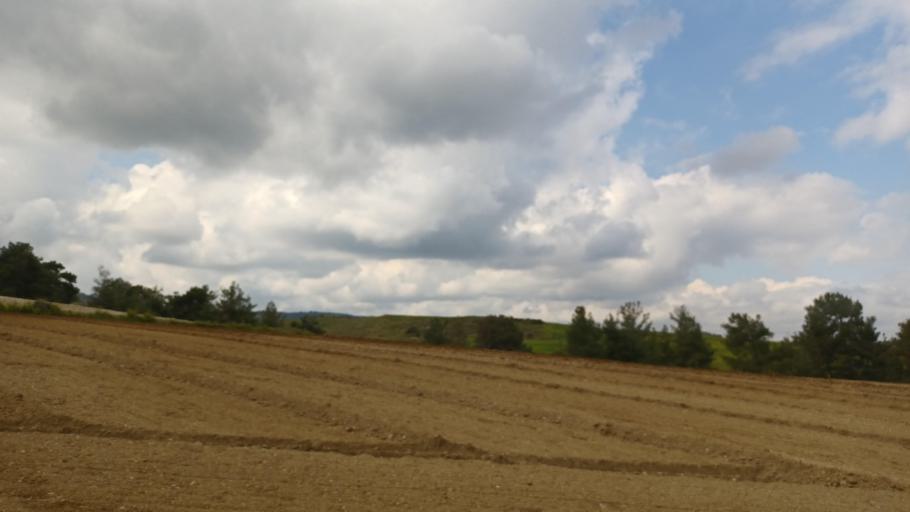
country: CY
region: Lefkosia
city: Kakopetria
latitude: 35.0756
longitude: 32.9572
